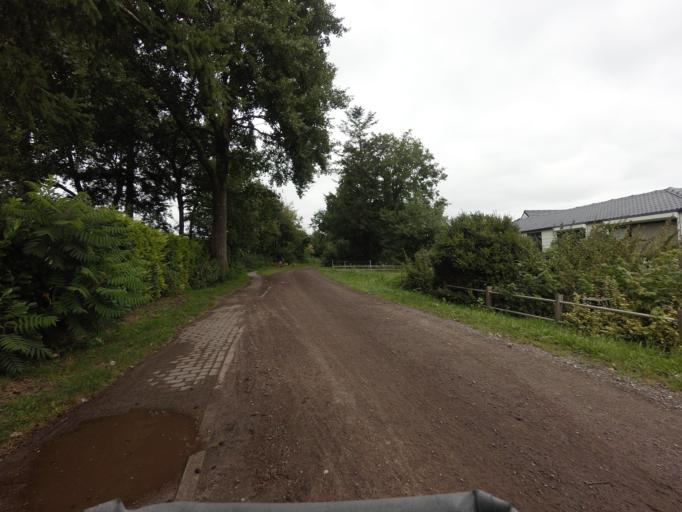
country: NL
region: Overijssel
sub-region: Gemeente Steenwijkerland
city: Steenwijk
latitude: 52.8123
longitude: 6.1227
